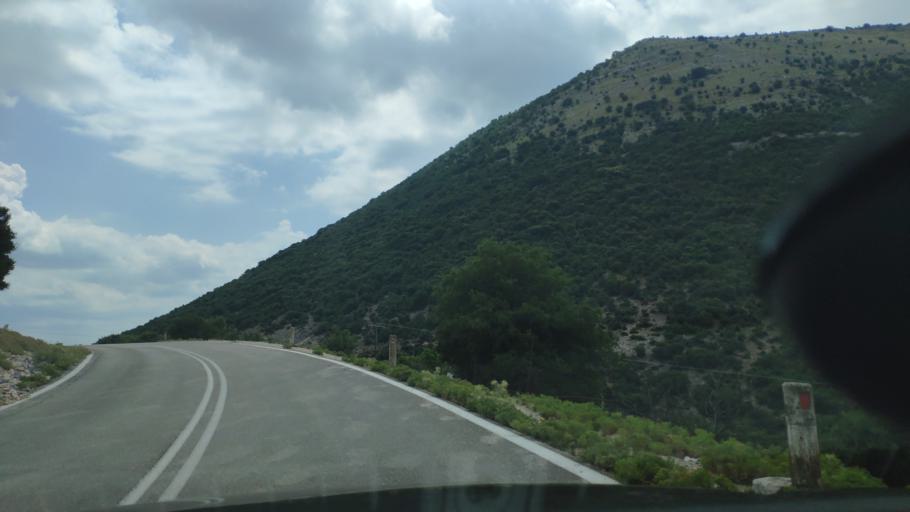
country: GR
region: Epirus
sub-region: Nomos Artas
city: Kampi
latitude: 39.2756
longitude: 20.9617
